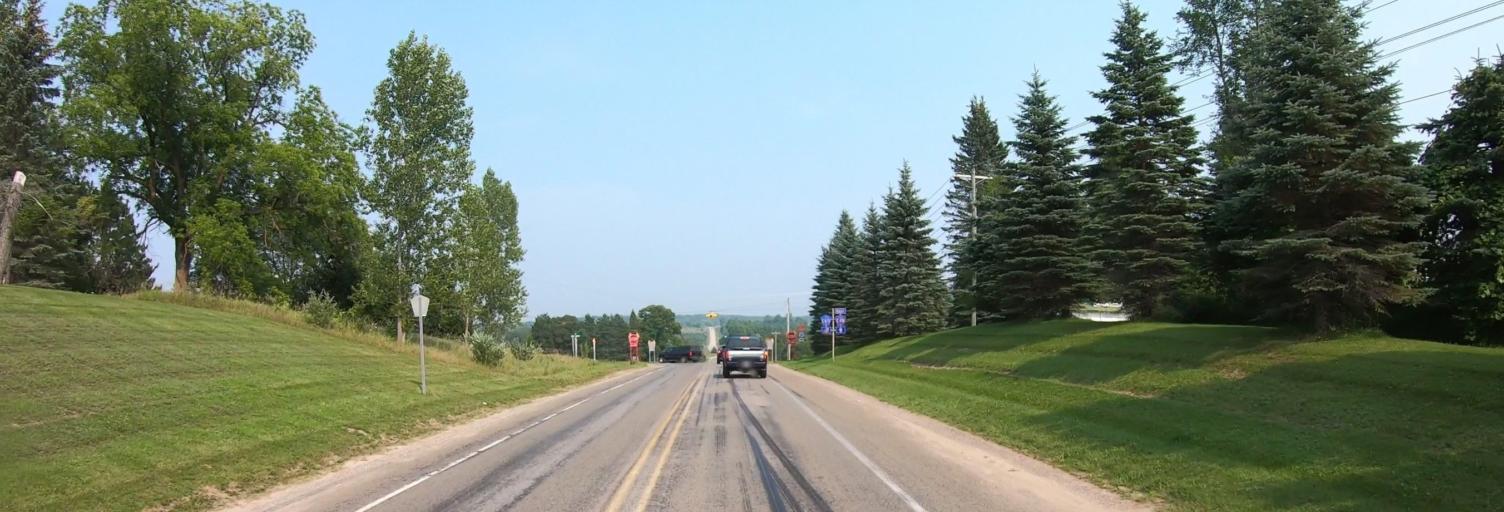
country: US
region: Michigan
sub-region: Charlevoix County
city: Charlevoix
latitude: 45.1840
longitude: -85.2652
